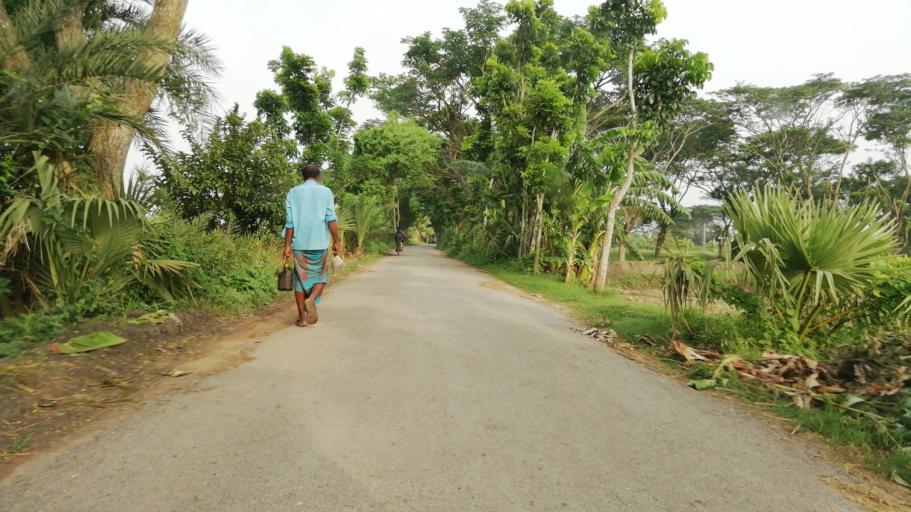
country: BD
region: Khulna
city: Bhatpara Abhaynagar
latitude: 23.0400
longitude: 89.3215
